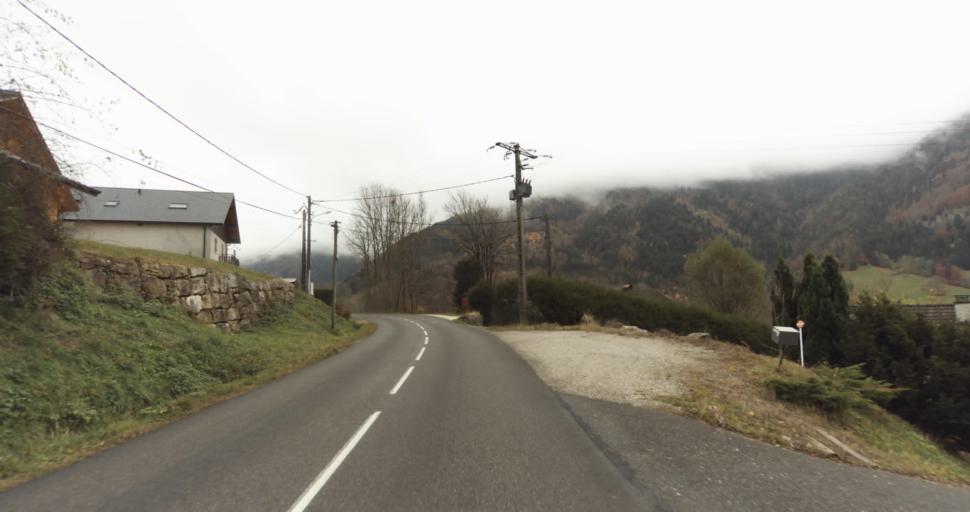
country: FR
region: Rhone-Alpes
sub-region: Departement de la Haute-Savoie
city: Thorens-Glieres
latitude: 45.9808
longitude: 6.2831
